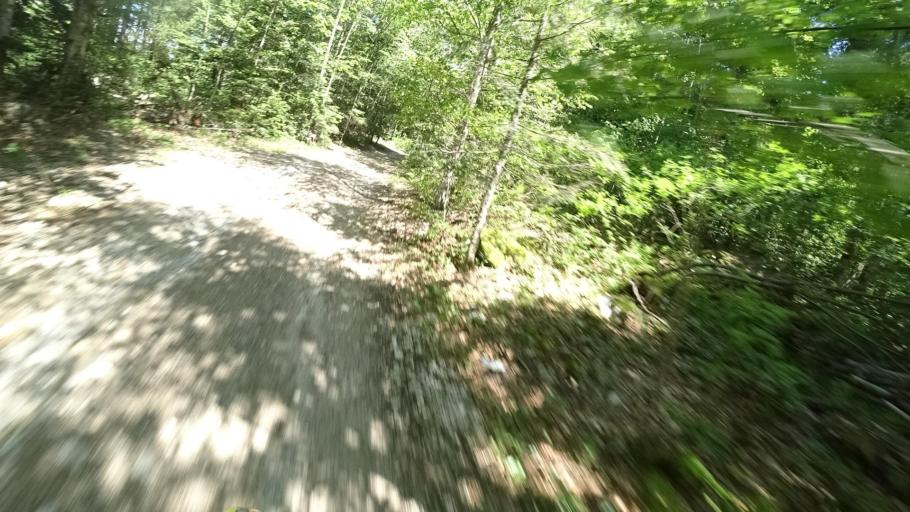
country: BA
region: Federation of Bosnia and Herzegovina
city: Stijena
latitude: 44.8114
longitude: 16.0406
